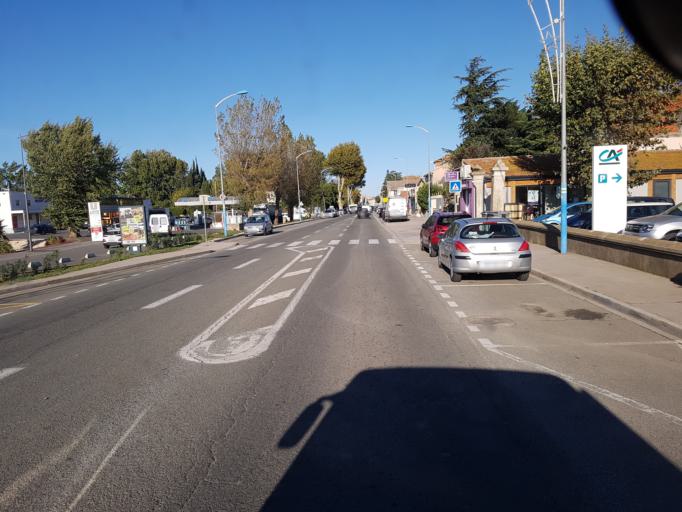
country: FR
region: Languedoc-Roussillon
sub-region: Departement de l'Aude
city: Coursan
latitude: 43.2288
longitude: 3.0510
